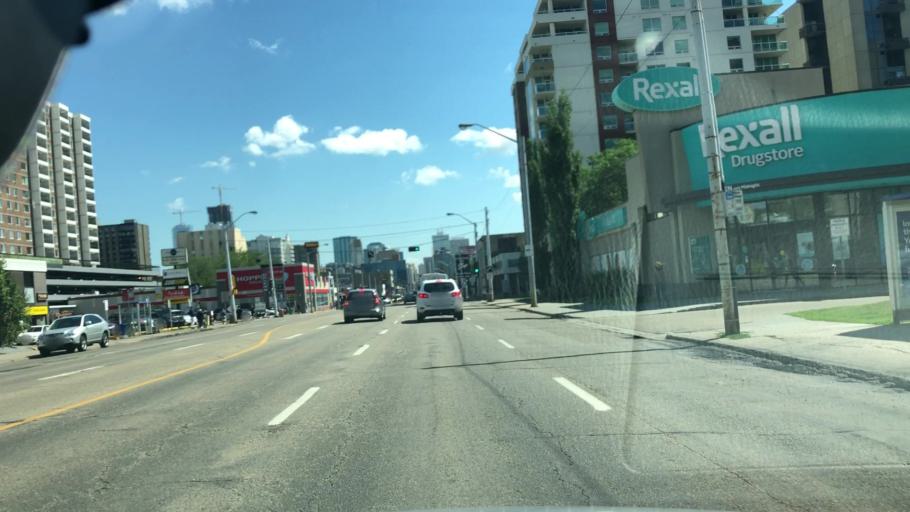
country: CA
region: Alberta
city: Edmonton
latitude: 53.5410
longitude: -113.5263
